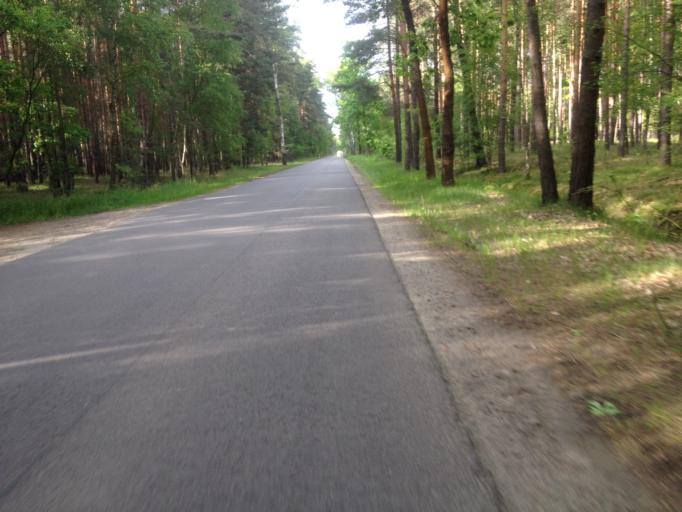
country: DE
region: Brandenburg
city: Cottbus
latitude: 51.8067
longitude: 14.3133
